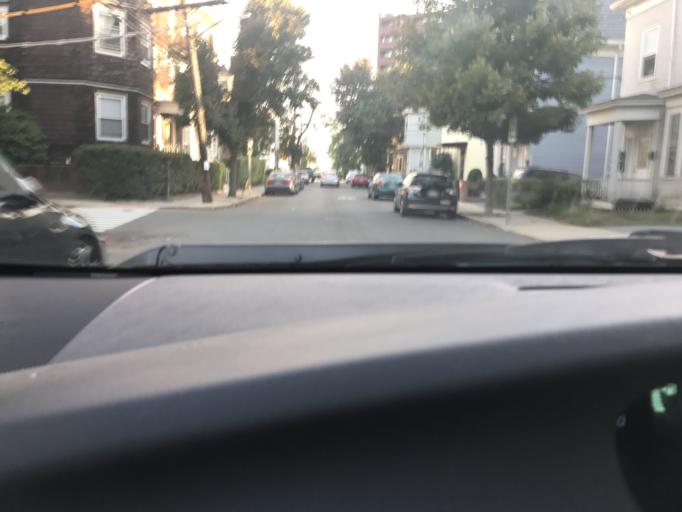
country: US
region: Massachusetts
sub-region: Middlesex County
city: Somerville
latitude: 42.3844
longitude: -71.0947
